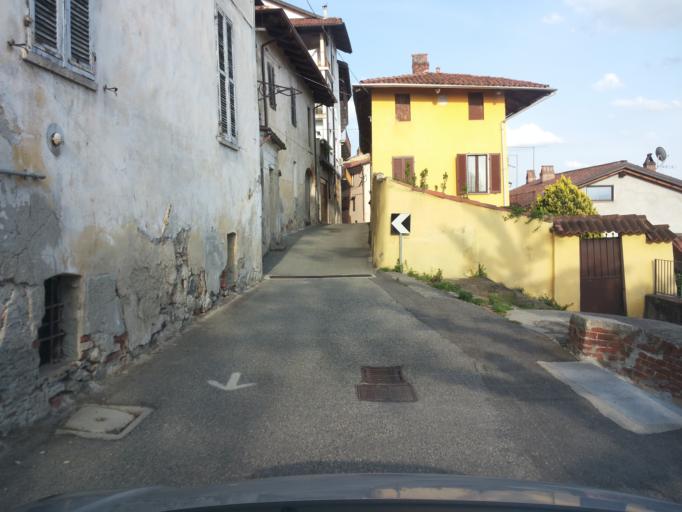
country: IT
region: Piedmont
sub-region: Provincia di Torino
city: Azeglio
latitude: 45.4245
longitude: 7.9943
